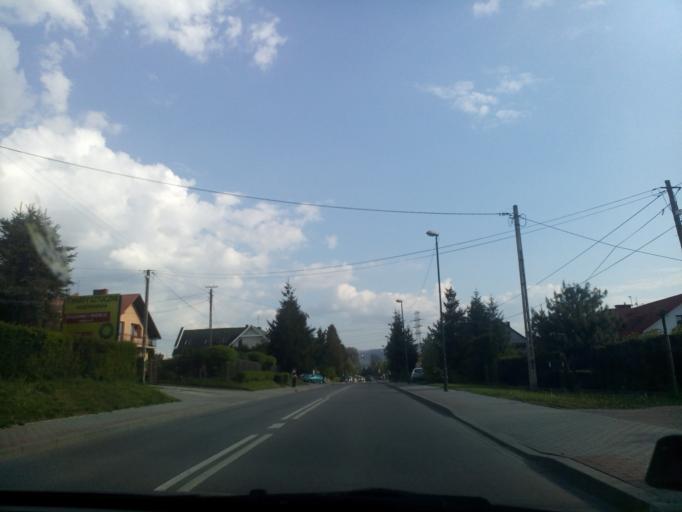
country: PL
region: Lesser Poland Voivodeship
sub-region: Powiat nowosadecki
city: Nawojowa
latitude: 49.5876
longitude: 20.7250
